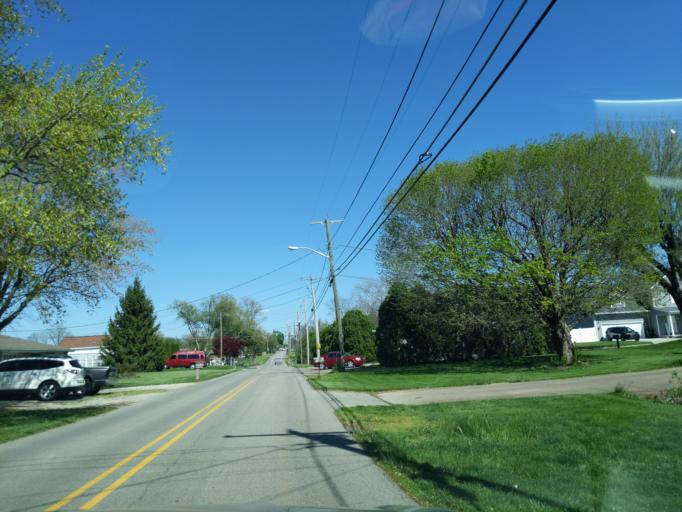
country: US
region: Indiana
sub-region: Decatur County
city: Greensburg
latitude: 39.3292
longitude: -85.4938
